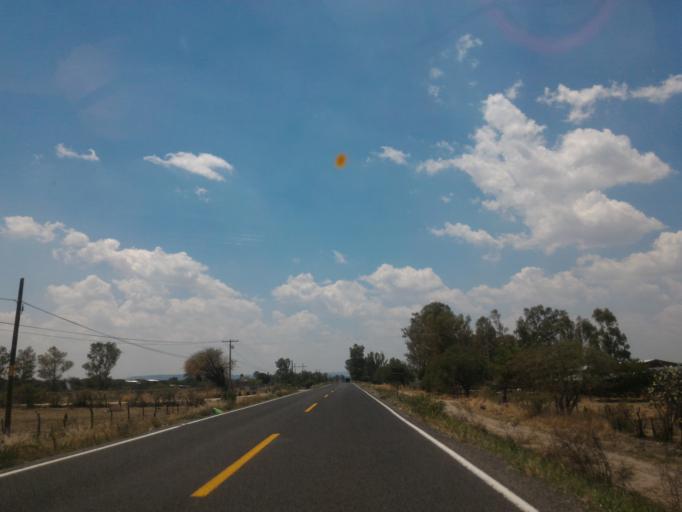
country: MX
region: Guanajuato
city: Ciudad Manuel Doblado
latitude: 20.7724
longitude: -101.9741
